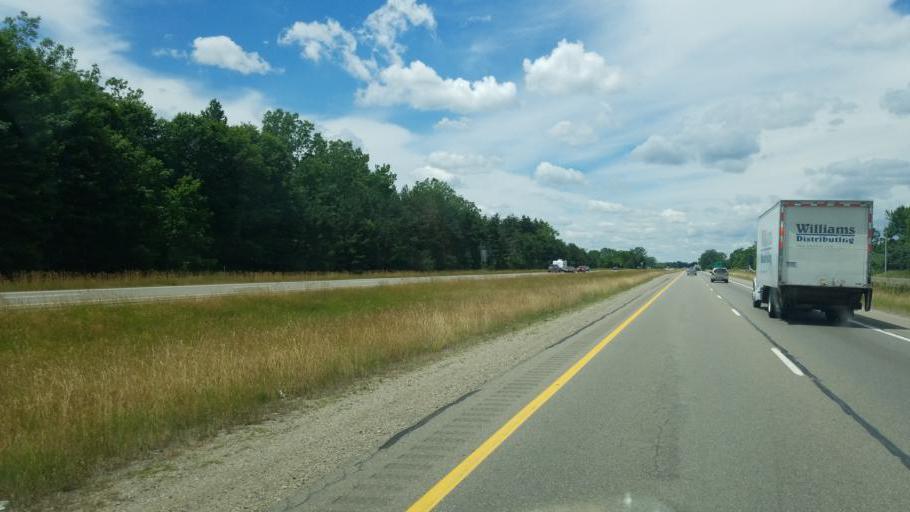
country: US
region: Michigan
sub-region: Ingham County
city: Holt
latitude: 42.6626
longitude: -84.5737
